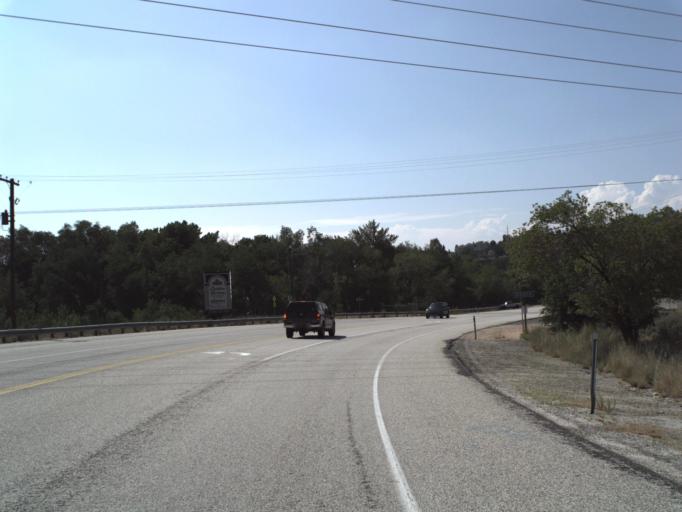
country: US
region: Utah
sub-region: Weber County
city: Ogden
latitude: 41.2362
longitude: -111.9244
